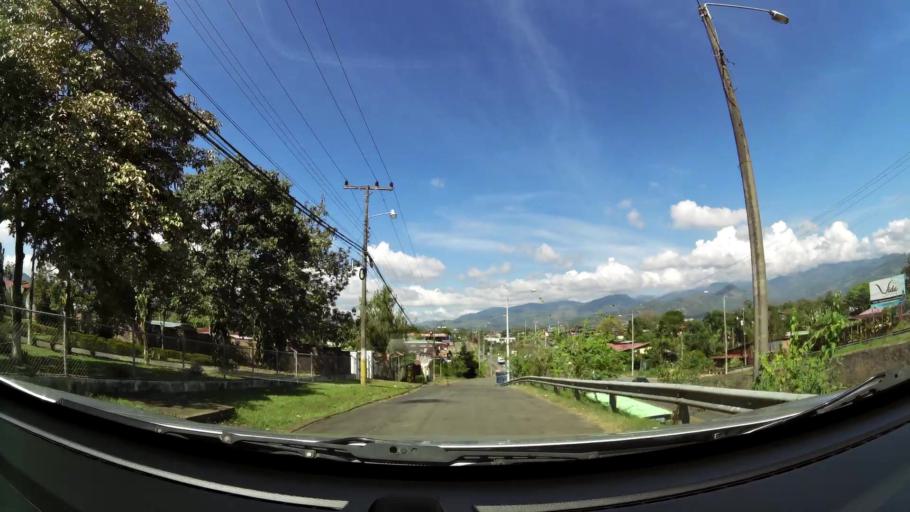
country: CR
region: San Jose
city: San Isidro
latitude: 9.3611
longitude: -83.6896
